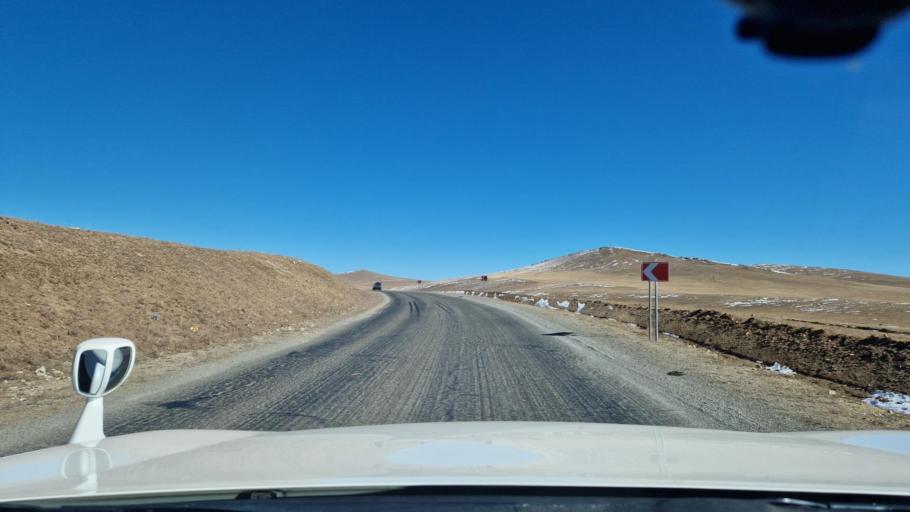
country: MN
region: Hentiy
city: Modot
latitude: 47.7967
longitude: 108.6922
